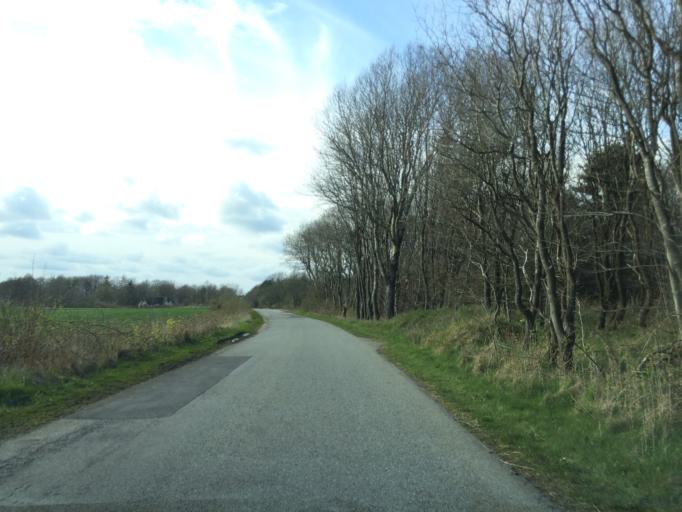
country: DK
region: Central Jutland
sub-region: Ringkobing-Skjern Kommune
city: Videbaek
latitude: 56.2046
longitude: 8.5509
